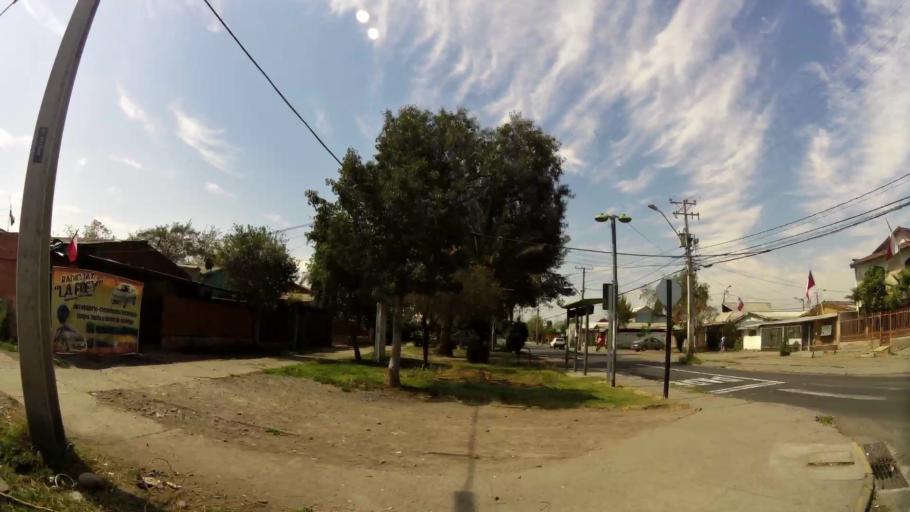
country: CL
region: Santiago Metropolitan
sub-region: Provincia de Santiago
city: La Pintana
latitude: -33.5538
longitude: -70.6571
